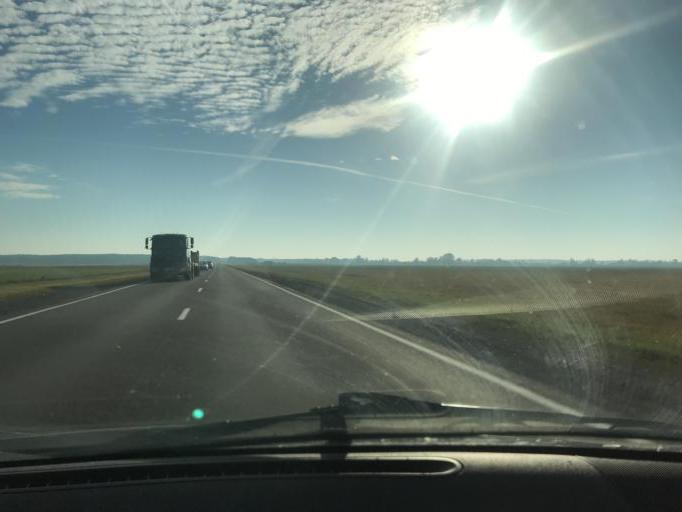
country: BY
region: Brest
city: Drahichyn
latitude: 52.1915
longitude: 25.2619
